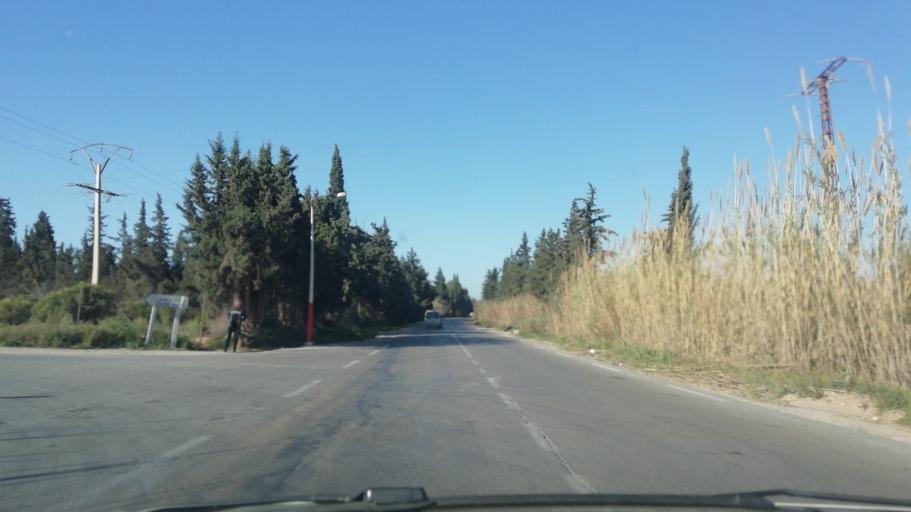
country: DZ
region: Mascara
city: Sig
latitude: 35.5730
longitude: -0.0182
